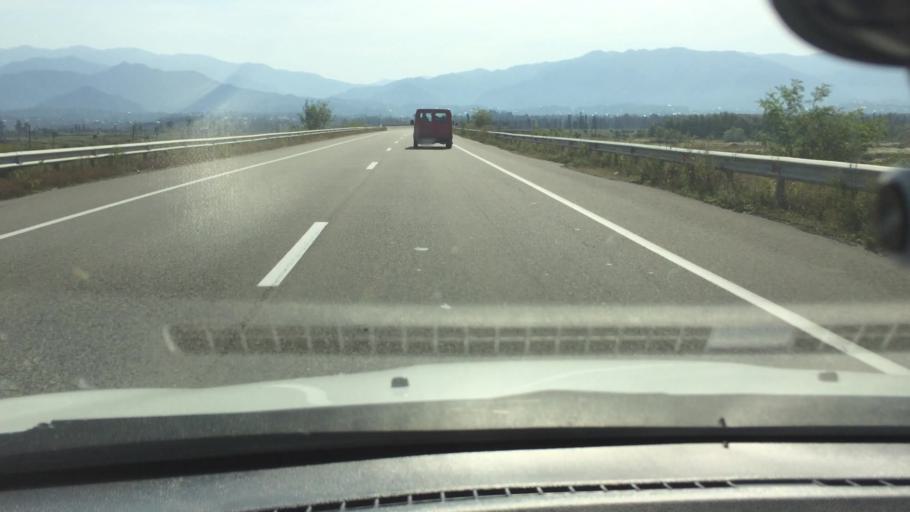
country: GE
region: Ajaria
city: Ochkhamuri
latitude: 41.8698
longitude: 41.8323
